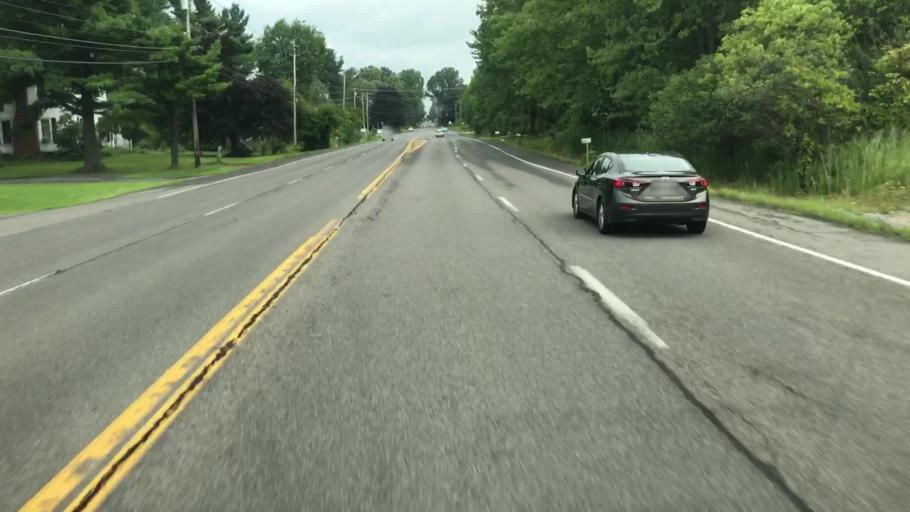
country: US
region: New York
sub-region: Onondaga County
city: Liverpool
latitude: 43.1479
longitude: -76.2073
